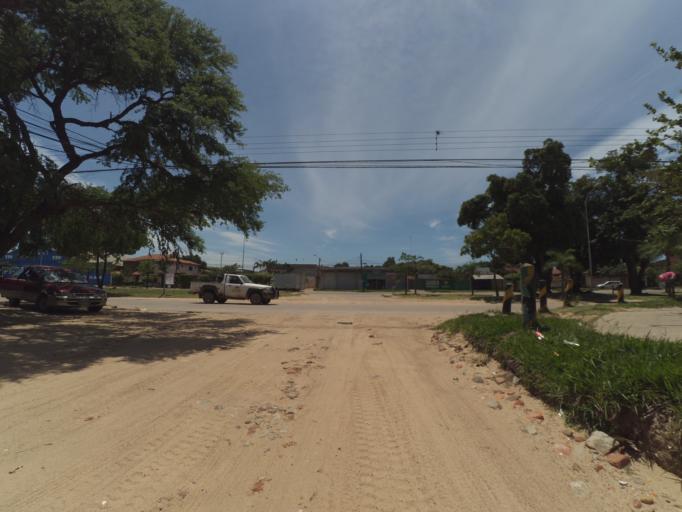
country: BO
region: Santa Cruz
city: Santa Cruz de la Sierra
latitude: -17.8135
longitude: -63.2216
